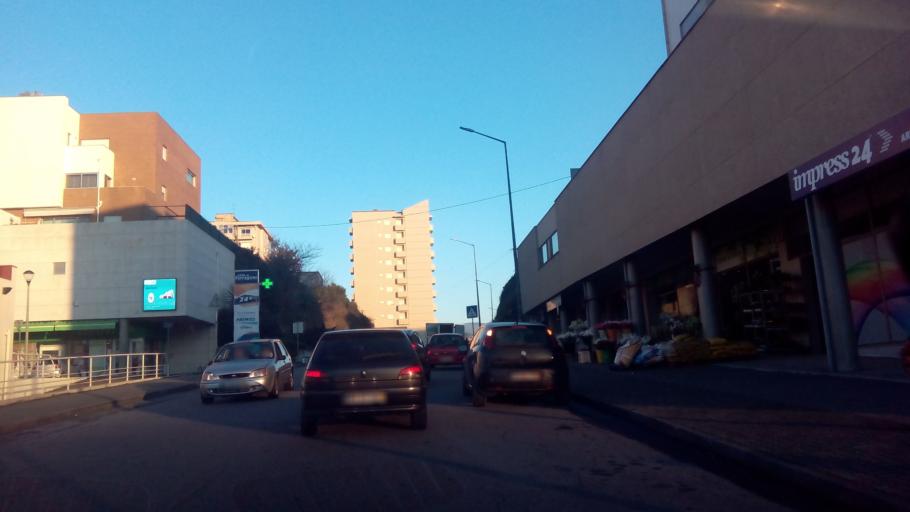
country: PT
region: Porto
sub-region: Amarante
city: Amarante
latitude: 41.2740
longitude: -8.0863
